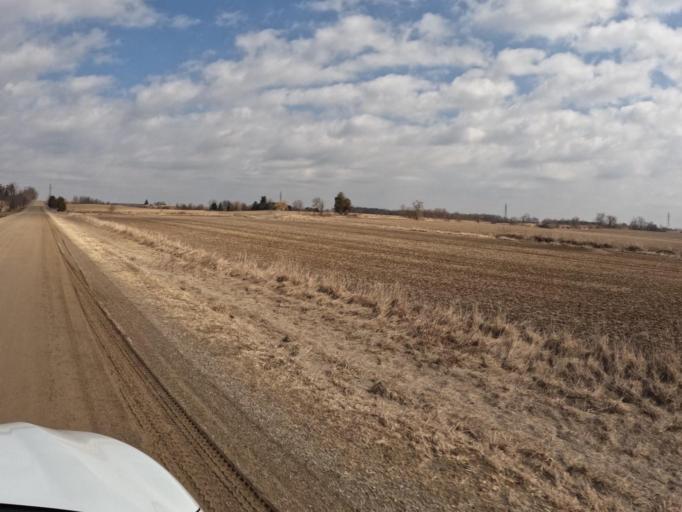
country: CA
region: Ontario
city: Orangeville
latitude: 43.9331
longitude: -80.2422
